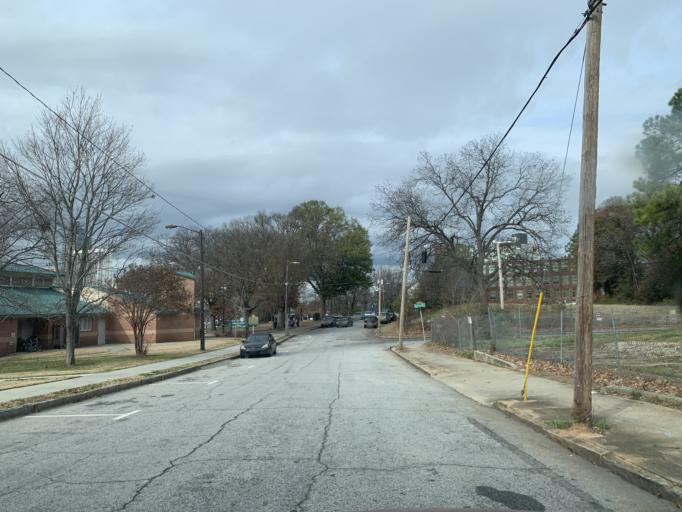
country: US
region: Georgia
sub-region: Fulton County
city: Atlanta
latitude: 33.7524
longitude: -84.3754
